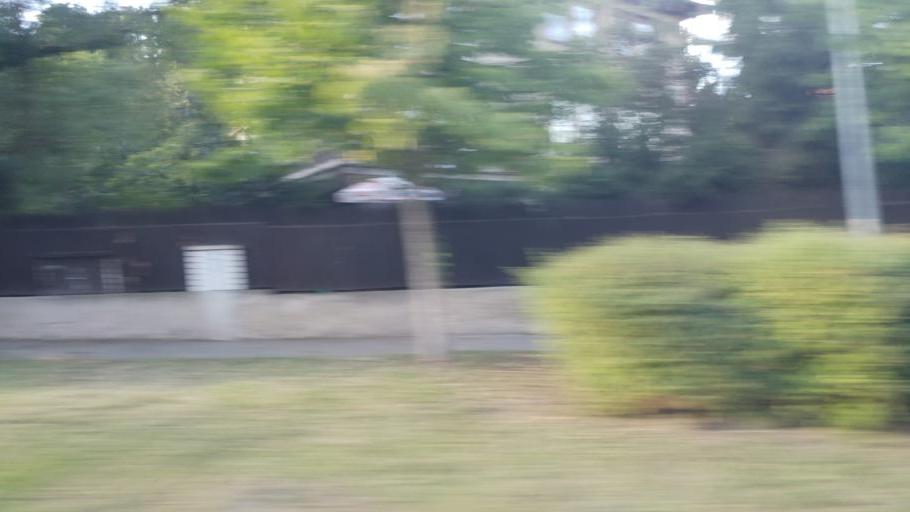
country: CZ
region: Praha
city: Prague
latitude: 50.1172
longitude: 14.4192
